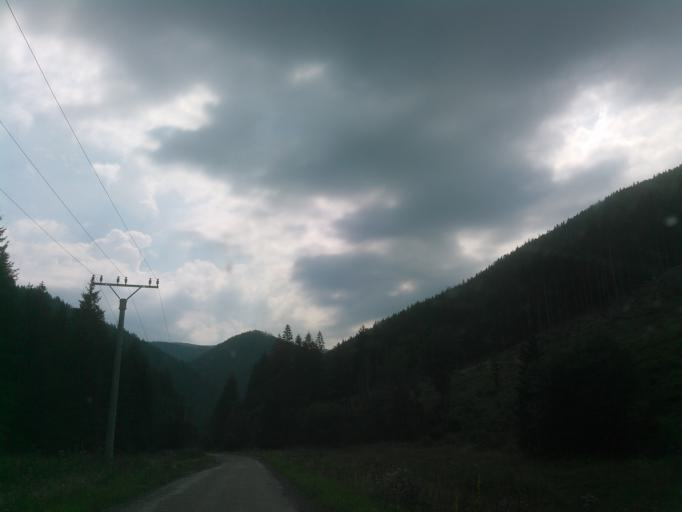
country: SK
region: Zilinsky
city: Ruzomberok
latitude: 48.9962
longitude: 19.4184
